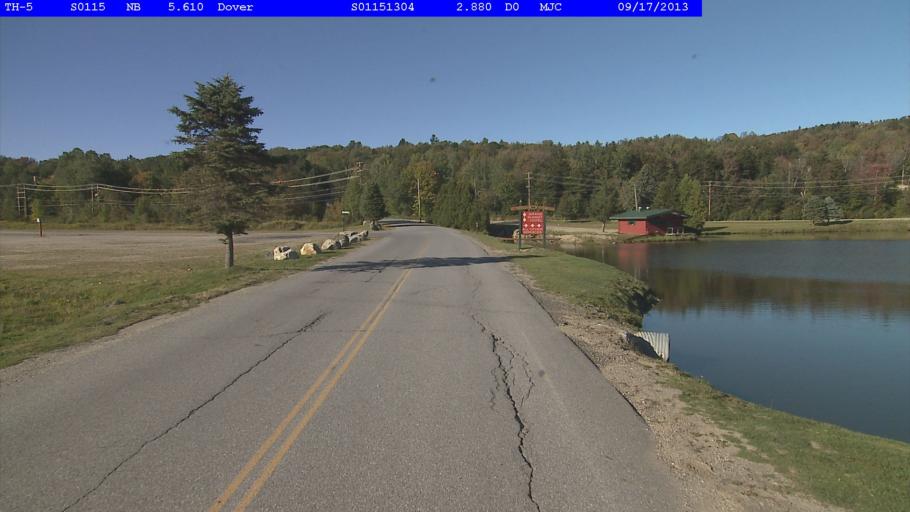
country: US
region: Vermont
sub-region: Windham County
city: Dover
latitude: 42.9656
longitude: -72.8900
